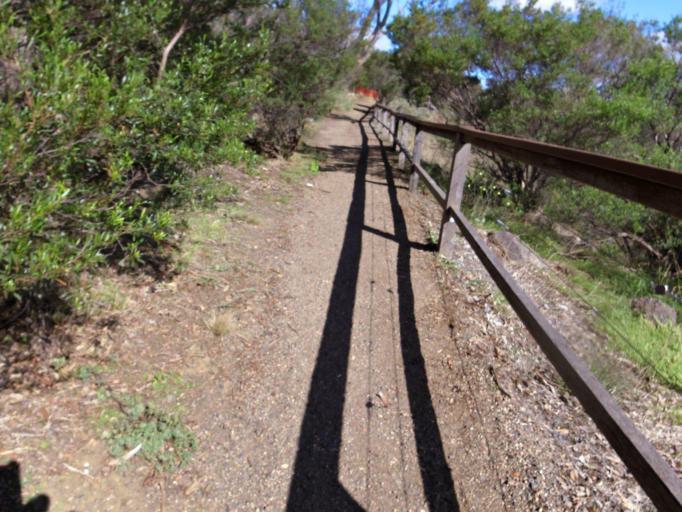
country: AU
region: Victoria
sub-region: Greater Geelong
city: Wandana Heights
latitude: -38.1509
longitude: 144.3086
